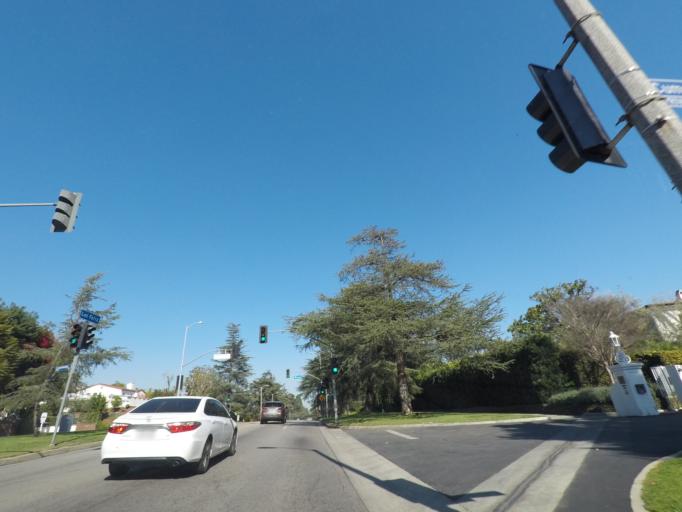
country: US
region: California
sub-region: Los Angeles County
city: Hollywood
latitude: 34.1092
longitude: -118.3022
